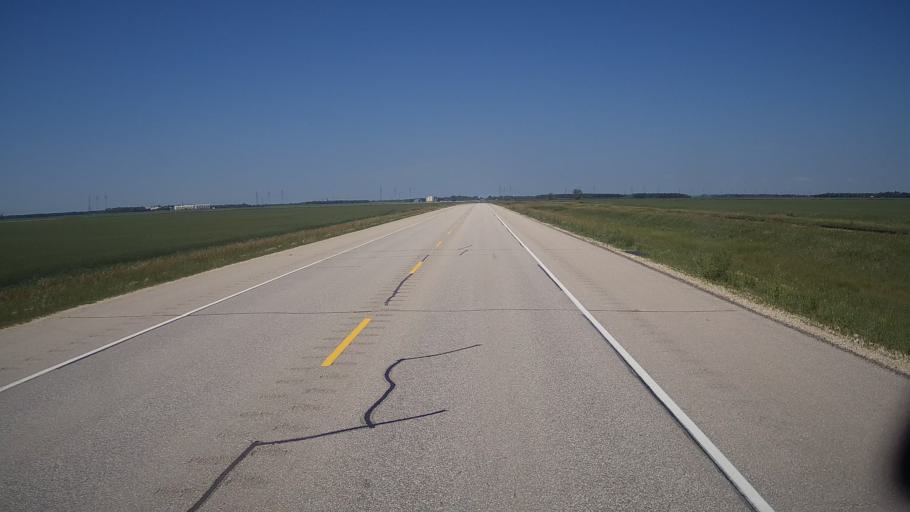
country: CA
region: Manitoba
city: Stonewall
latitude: 50.0380
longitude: -97.4024
